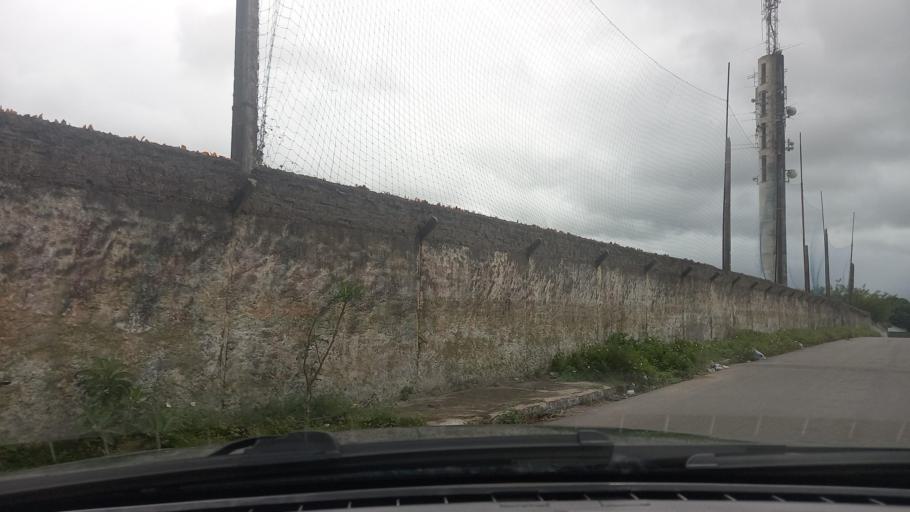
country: BR
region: Alagoas
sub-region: Delmiro Gouveia
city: Delmiro Gouveia
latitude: -9.3906
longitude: -37.9979
